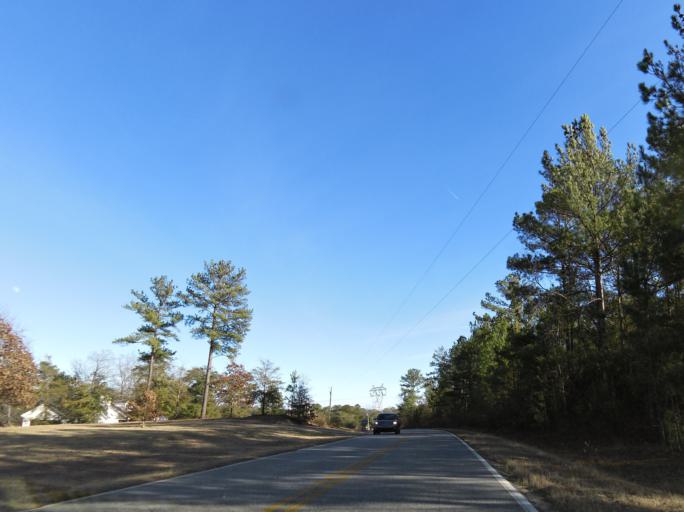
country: US
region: Georgia
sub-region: Bibb County
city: West Point
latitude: 32.7681
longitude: -83.8646
